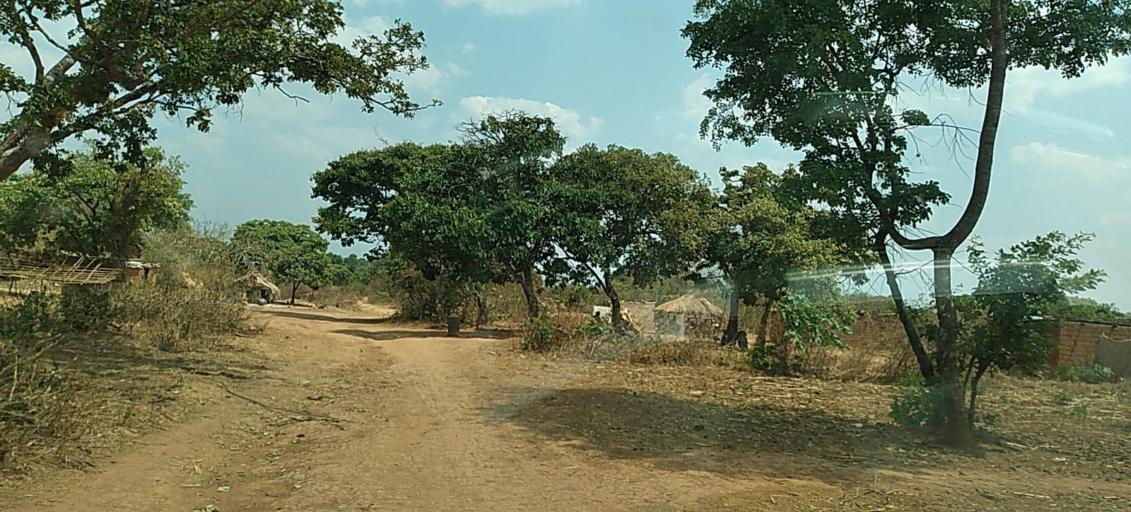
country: CD
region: Katanga
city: Kipushi
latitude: -12.0247
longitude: 27.4347
